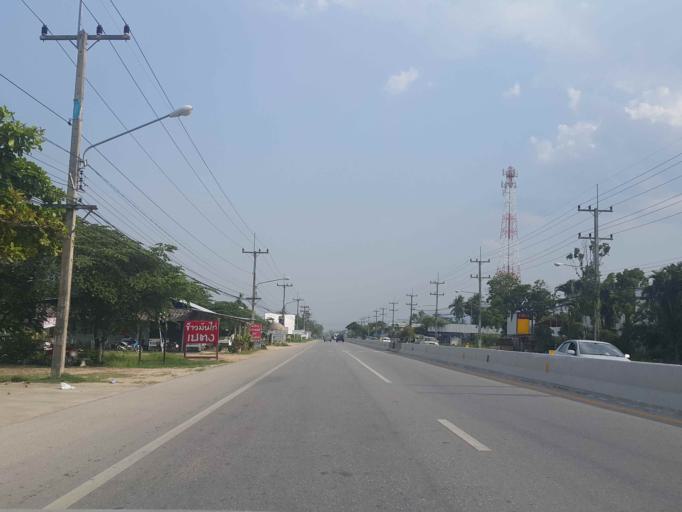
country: TH
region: Chiang Mai
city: Mae Taeng
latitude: 19.0164
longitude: 98.9445
